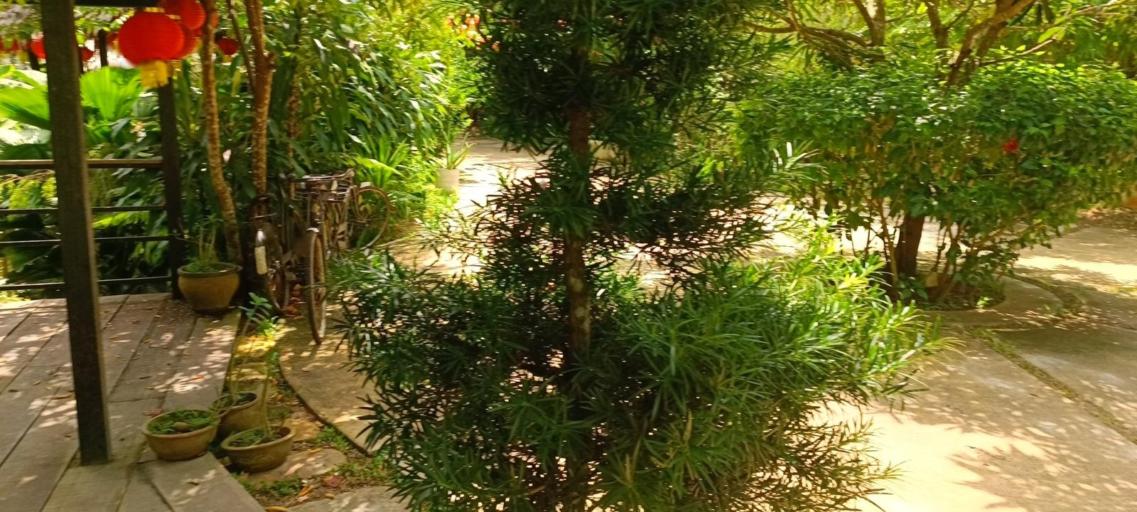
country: MY
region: Penang
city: Kampung Sungai Ara
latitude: 5.3185
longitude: 100.2425
